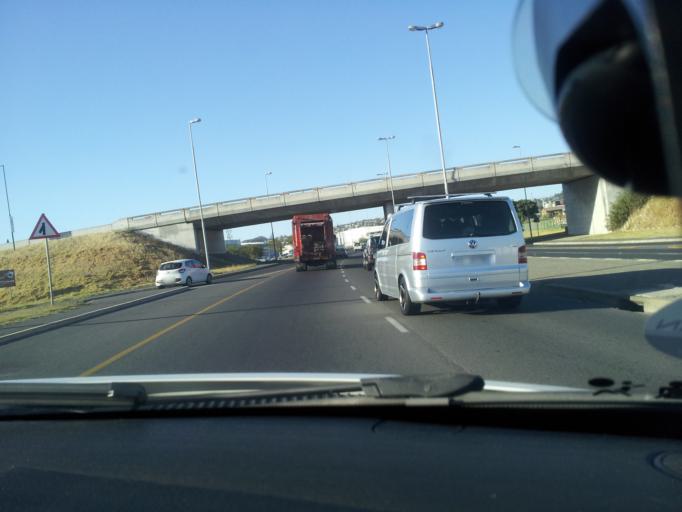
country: ZA
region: Western Cape
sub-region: Cape Winelands District Municipality
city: Stellenbosch
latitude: -34.0819
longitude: 18.8190
